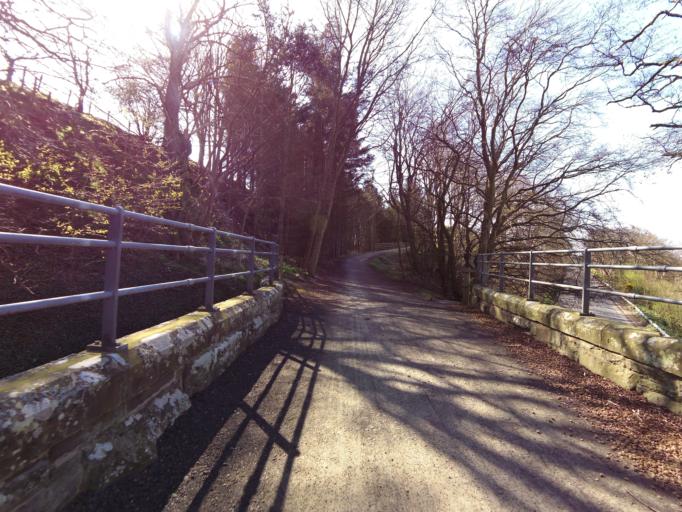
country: GB
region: Scotland
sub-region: Angus
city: Montrose
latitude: 56.7502
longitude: -2.4510
